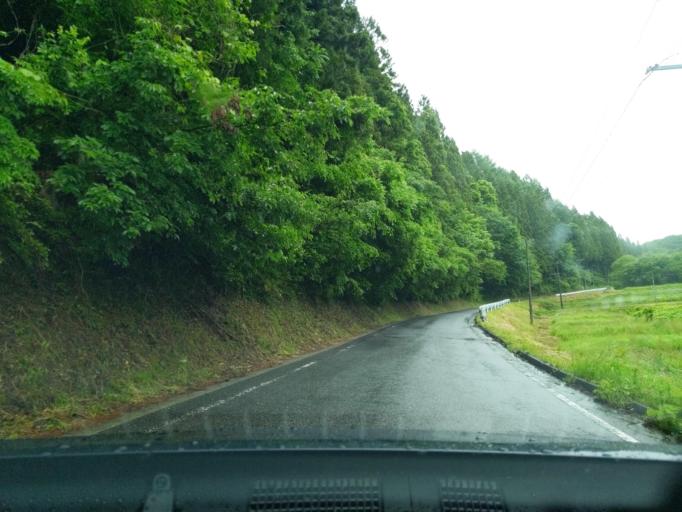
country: JP
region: Fukushima
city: Funehikimachi-funehiki
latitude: 37.5969
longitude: 140.6274
